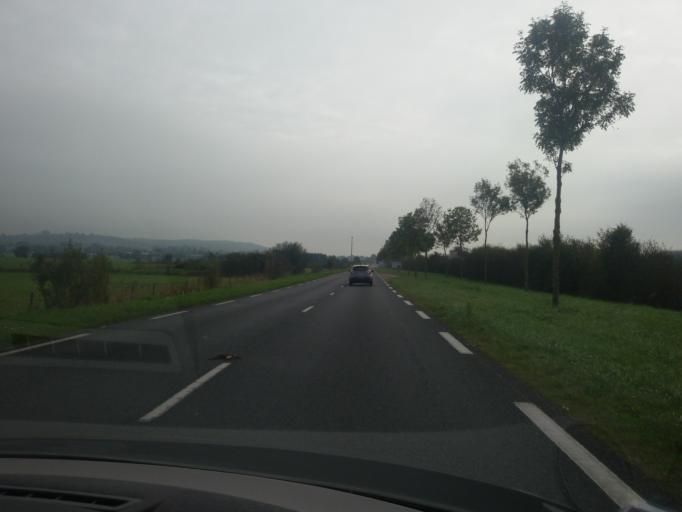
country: FR
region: Lower Normandy
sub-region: Departement du Calvados
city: Dives-sur-Mer
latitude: 49.2365
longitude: -0.0935
